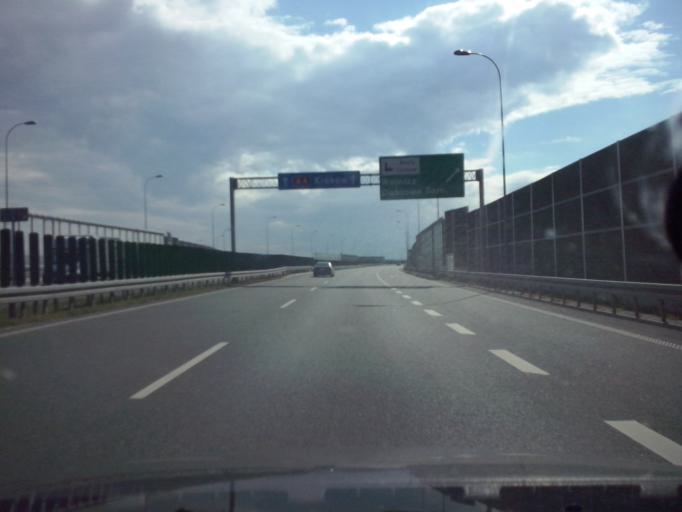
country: PL
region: Lesser Poland Voivodeship
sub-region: Powiat tarnowski
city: Wierzchoslawice
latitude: 50.0167
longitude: 20.8706
